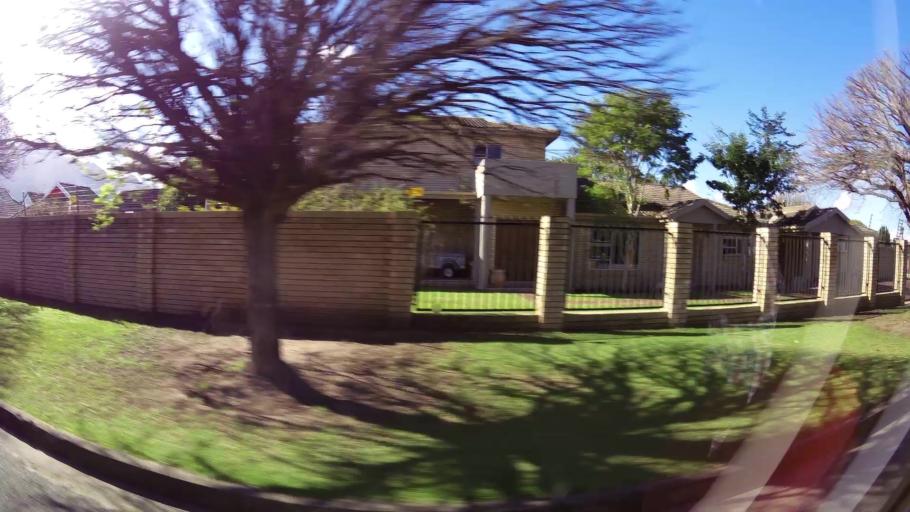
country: ZA
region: Western Cape
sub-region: Eden District Municipality
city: George
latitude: -33.9535
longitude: 22.4324
